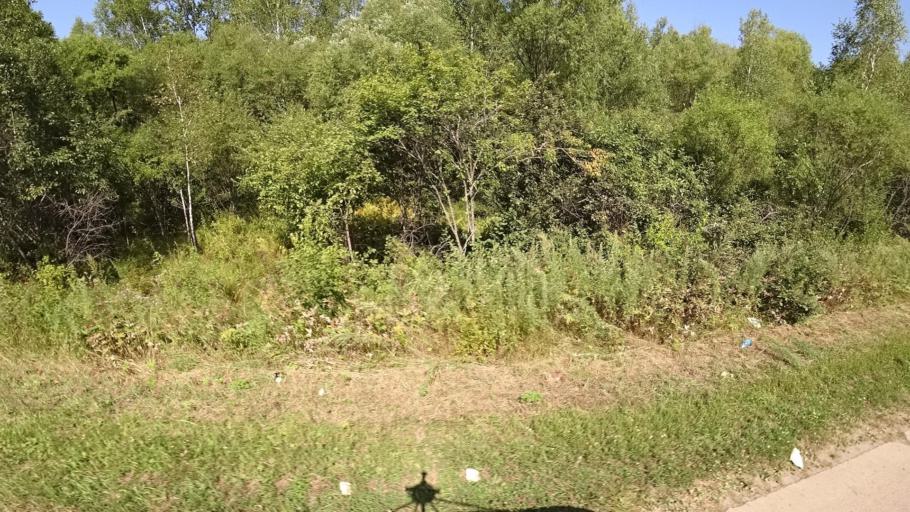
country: RU
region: Khabarovsk Krai
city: Khor
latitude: 47.9787
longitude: 135.1010
